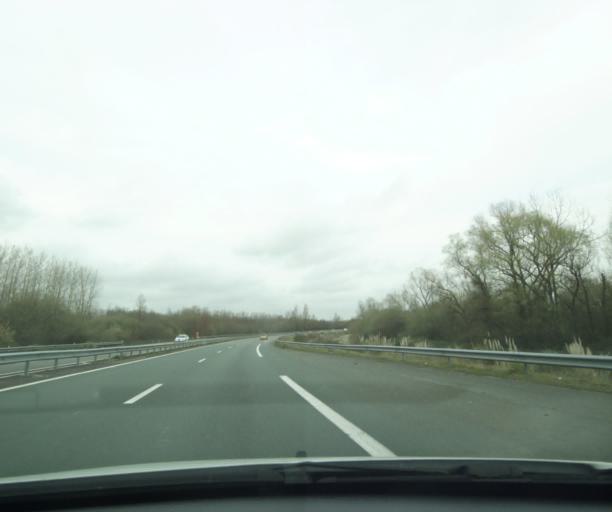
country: FR
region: Aquitaine
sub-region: Departement des Pyrenees-Atlantiques
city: Bardos
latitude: 43.5261
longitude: -1.2051
